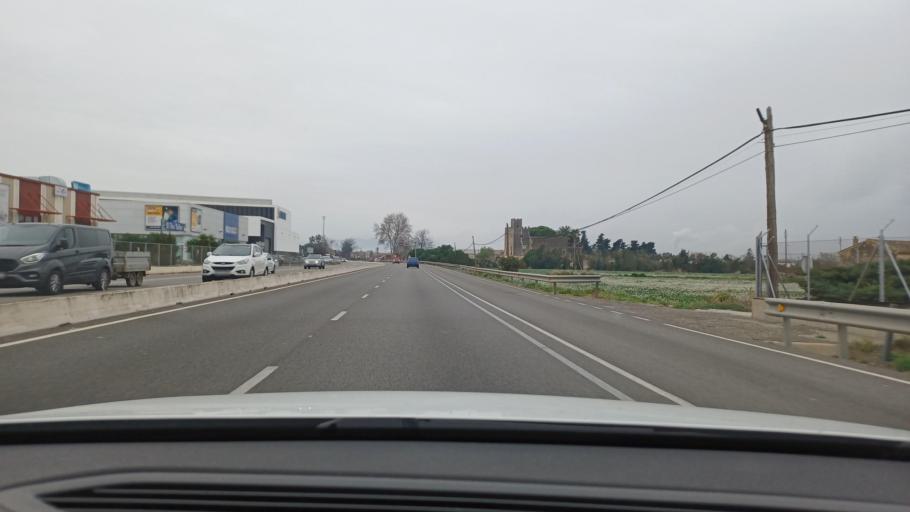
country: ES
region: Catalonia
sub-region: Provincia de Tarragona
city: Tortosa
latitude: 40.7961
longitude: 0.5206
